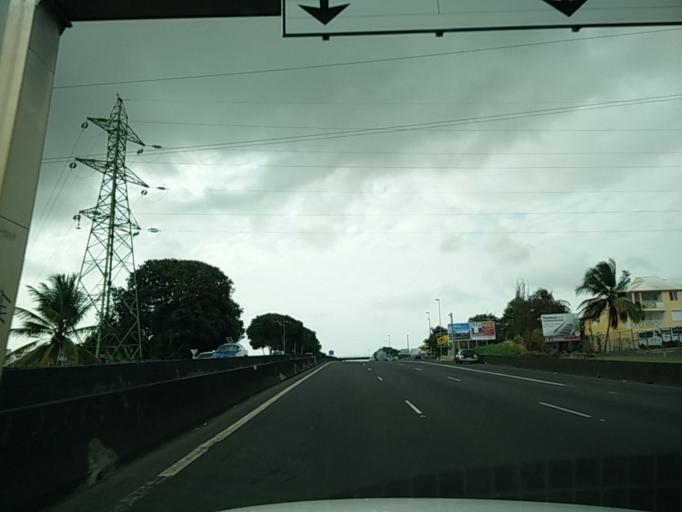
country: GP
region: Guadeloupe
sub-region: Guadeloupe
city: Baie-Mahault
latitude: 16.2378
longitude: -61.5888
